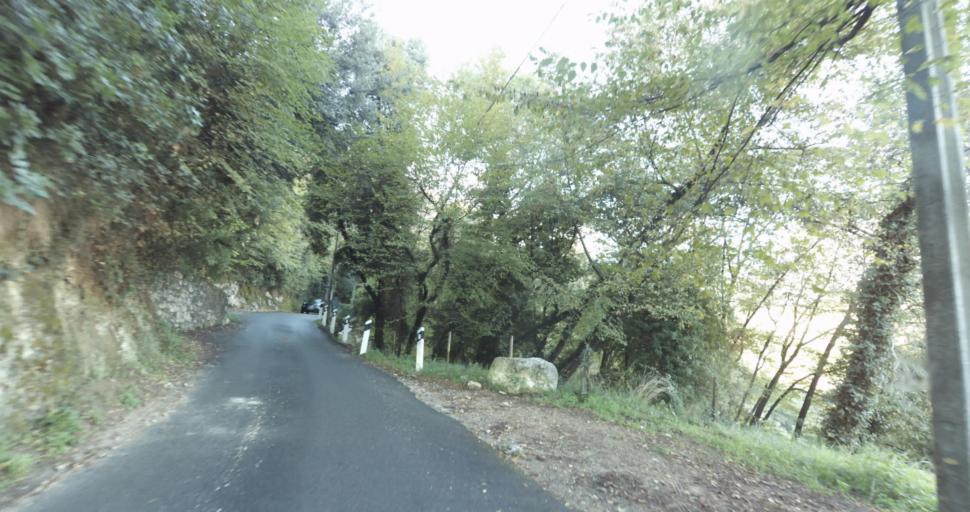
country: FR
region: Provence-Alpes-Cote d'Azur
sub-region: Departement des Alpes-Maritimes
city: La Gaude
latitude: 43.7174
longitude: 7.1348
